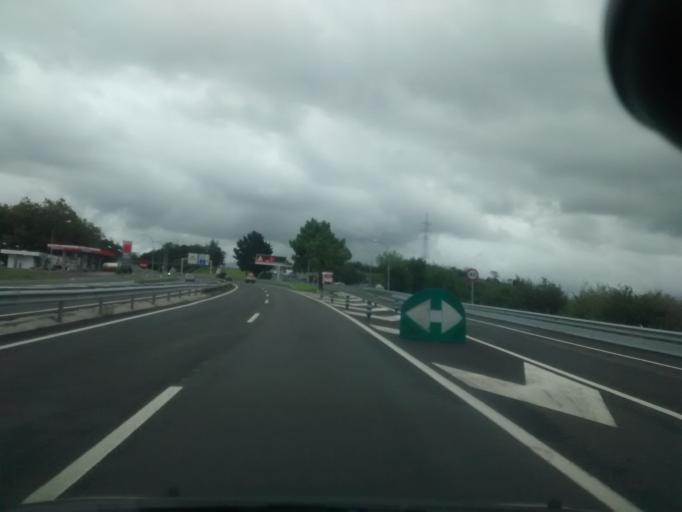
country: ES
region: Basque Country
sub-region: Provincia de Guipuzcoa
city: Usurbil
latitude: 43.2871
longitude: -2.0341
